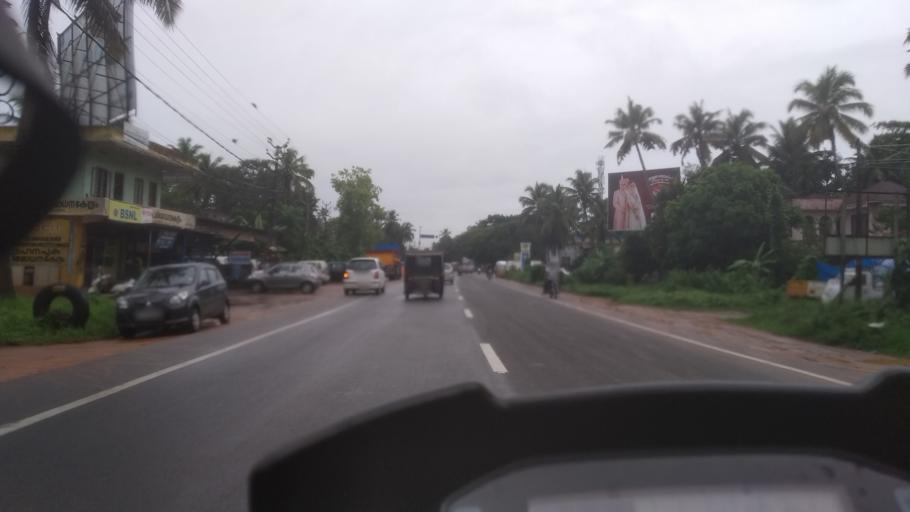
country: IN
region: Kerala
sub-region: Alappuzha
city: Kayankulam
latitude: 9.1559
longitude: 76.5095
